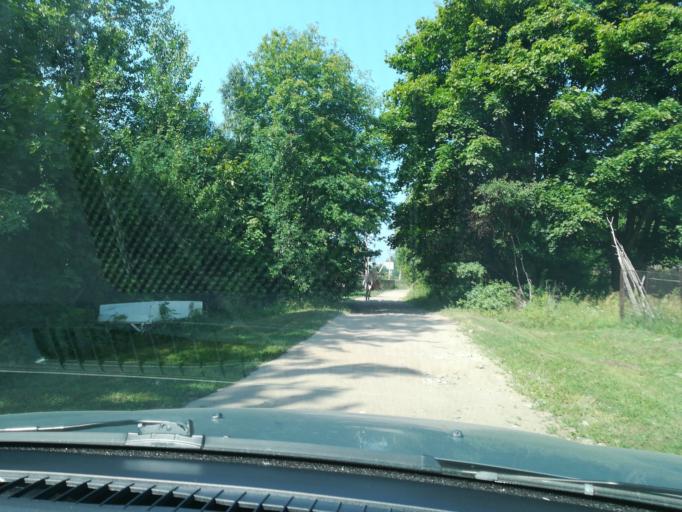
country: RU
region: Leningrad
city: Ust'-Luga
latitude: 59.7589
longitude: 28.1864
